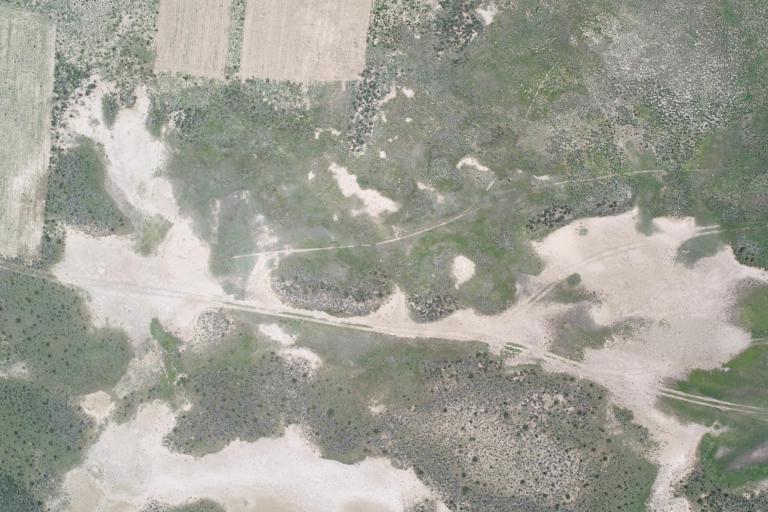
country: BO
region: La Paz
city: Curahuara de Carangas
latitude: -17.3214
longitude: -68.5154
